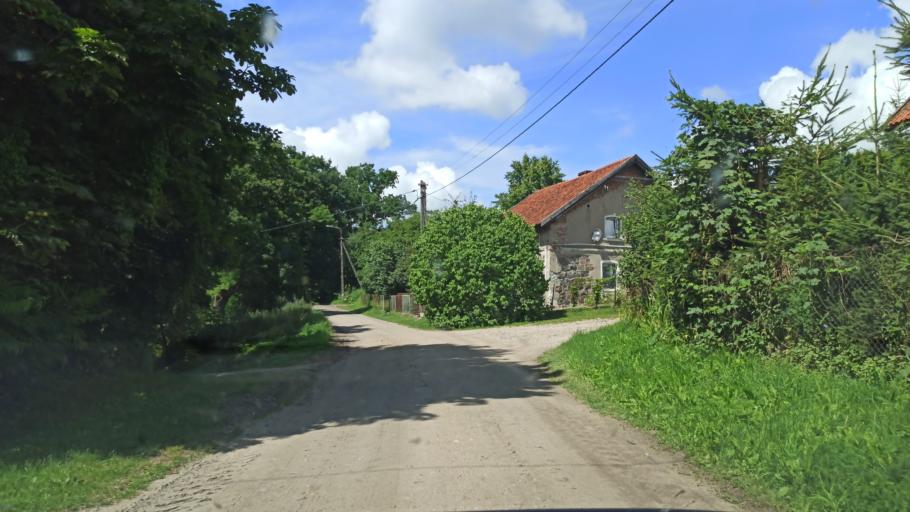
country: PL
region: Warmian-Masurian Voivodeship
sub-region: Powiat ostrodzki
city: Milakowo
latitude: 53.8601
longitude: 20.0647
